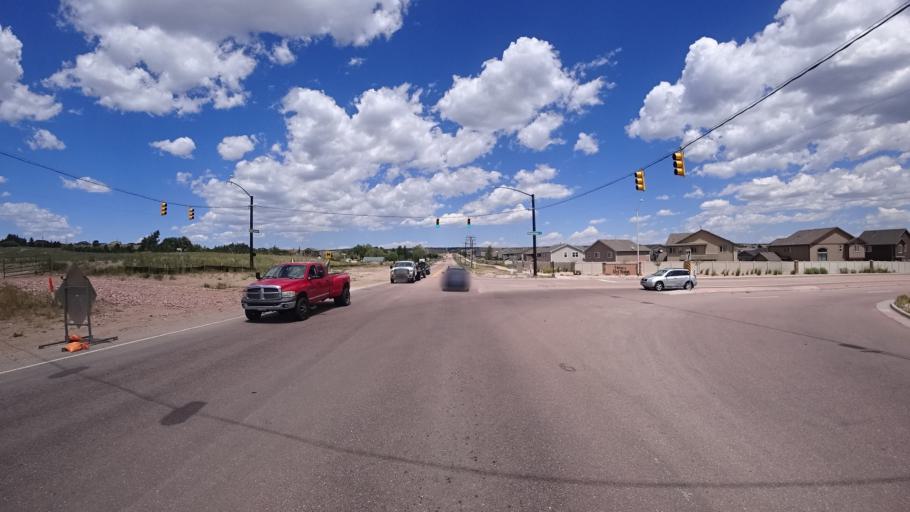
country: US
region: Colorado
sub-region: El Paso County
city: Black Forest
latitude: 38.9435
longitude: -104.7010
